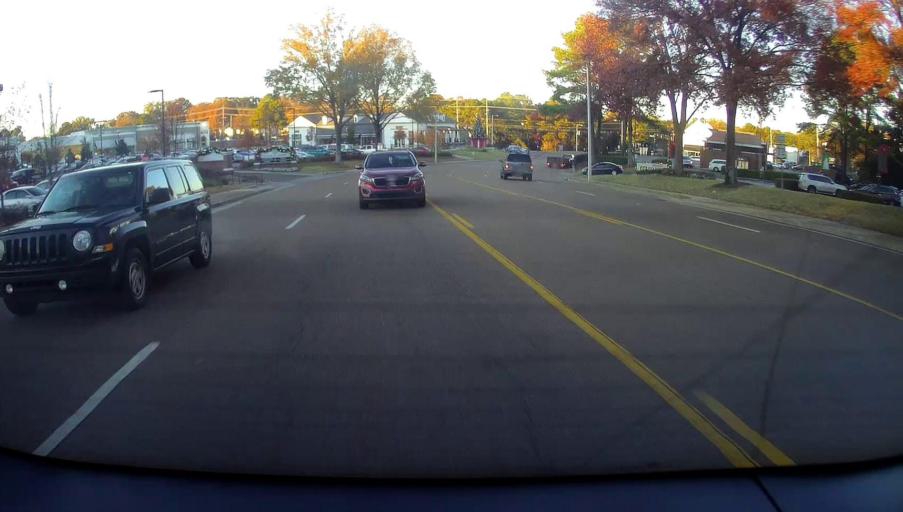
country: US
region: Tennessee
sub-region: Shelby County
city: Germantown
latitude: 35.0925
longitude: -89.8119
